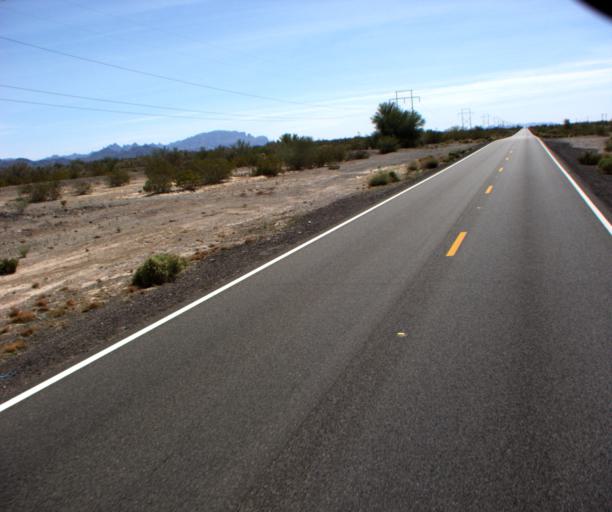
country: US
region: Arizona
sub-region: La Paz County
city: Quartzsite
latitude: 33.5726
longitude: -114.2171
